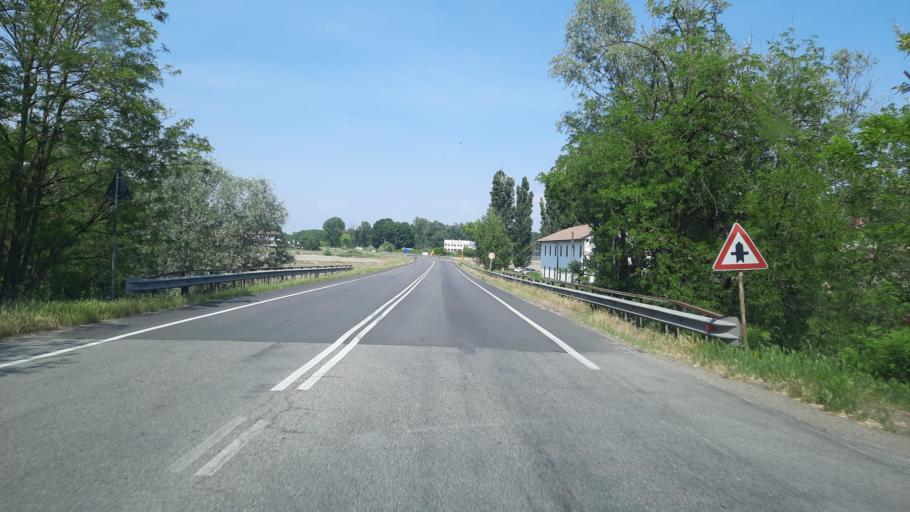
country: IT
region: Lombardy
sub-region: Provincia di Pavia
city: Mortara
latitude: 45.2453
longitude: 8.7512
